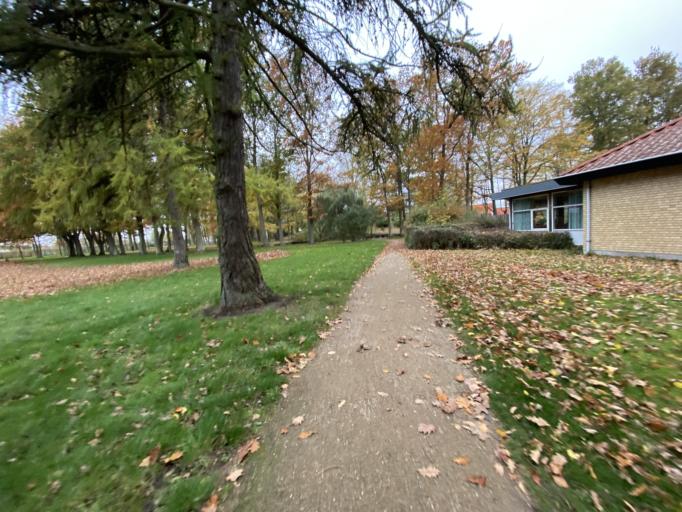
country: DK
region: Capital Region
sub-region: Dragor Kommune
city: Dragor
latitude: 55.5891
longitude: 12.6649
